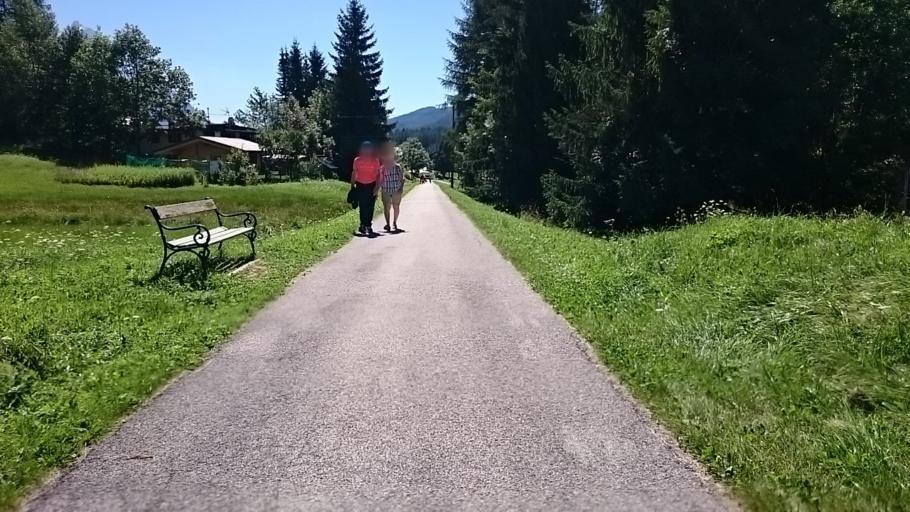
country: IT
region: Veneto
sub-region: Provincia di Belluno
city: Cortina d'Ampezzo
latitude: 46.5185
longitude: 12.1412
